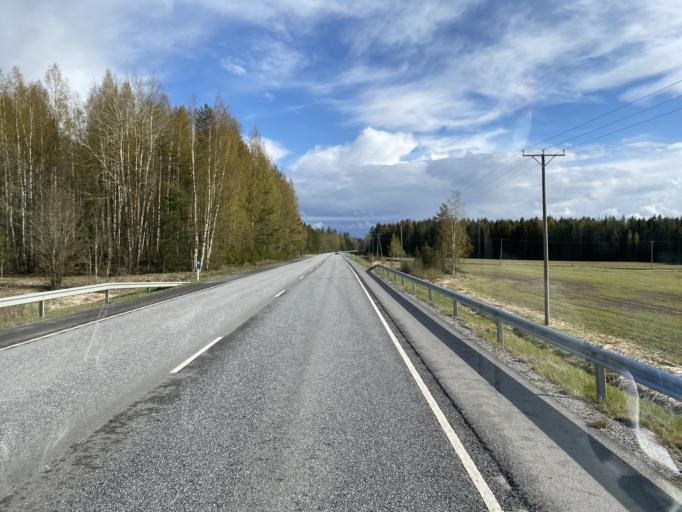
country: FI
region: Pirkanmaa
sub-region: Tampere
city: Lempaeaelae
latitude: 61.2796
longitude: 23.7454
